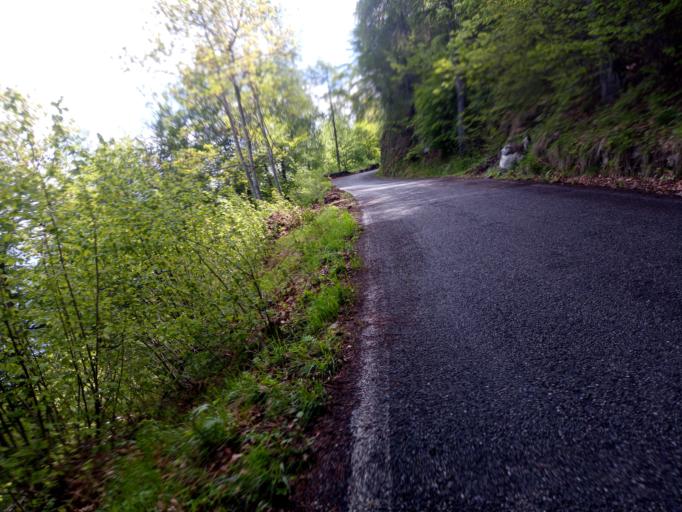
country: IT
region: Piedmont
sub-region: Provincia di Torino
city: Meana di Susa
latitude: 45.1080
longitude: 7.0680
